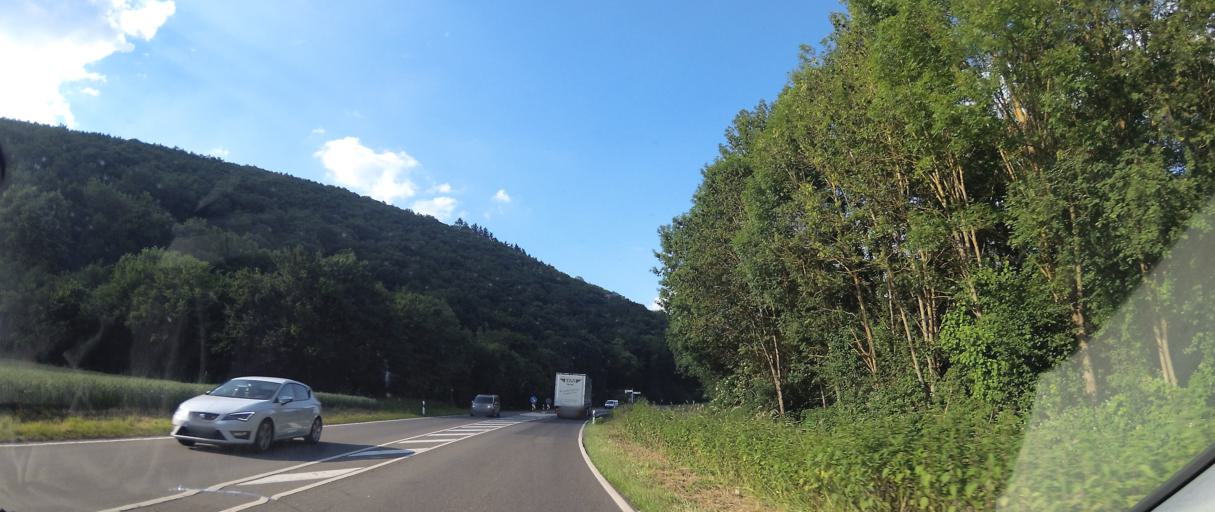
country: DE
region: Rheinland-Pfalz
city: Hochstatten
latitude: 49.7501
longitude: 7.8192
